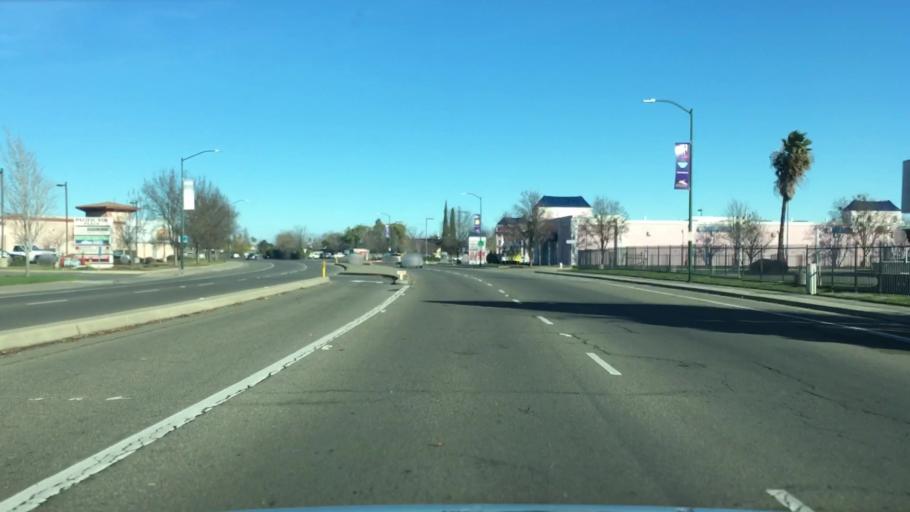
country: US
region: California
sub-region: Sacramento County
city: Florin
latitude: 38.5011
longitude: -121.4300
